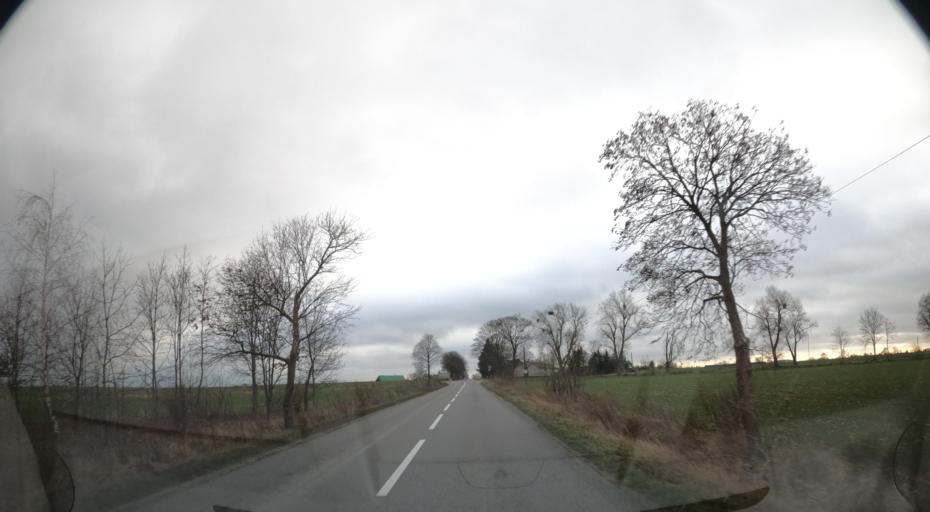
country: PL
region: Kujawsko-Pomorskie
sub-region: Powiat nakielski
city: Sadki
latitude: 53.1667
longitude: 17.4389
